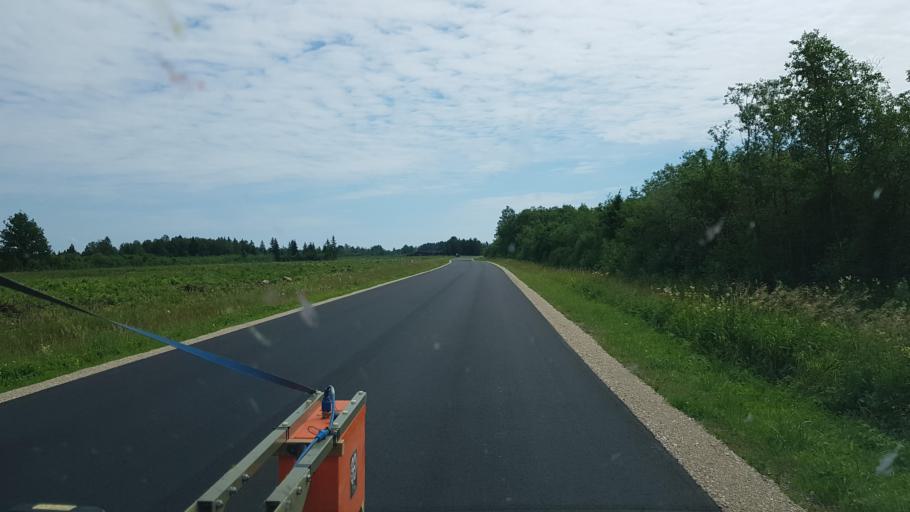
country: EE
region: Paernumaa
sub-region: Halinga vald
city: Parnu-Jaagupi
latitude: 58.6196
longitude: 24.2768
